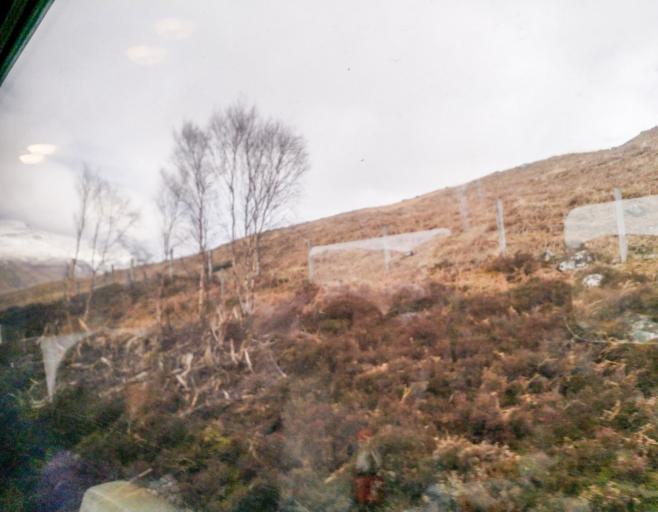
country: GB
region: Scotland
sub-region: Highland
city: Spean Bridge
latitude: 56.7777
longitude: -4.7314
